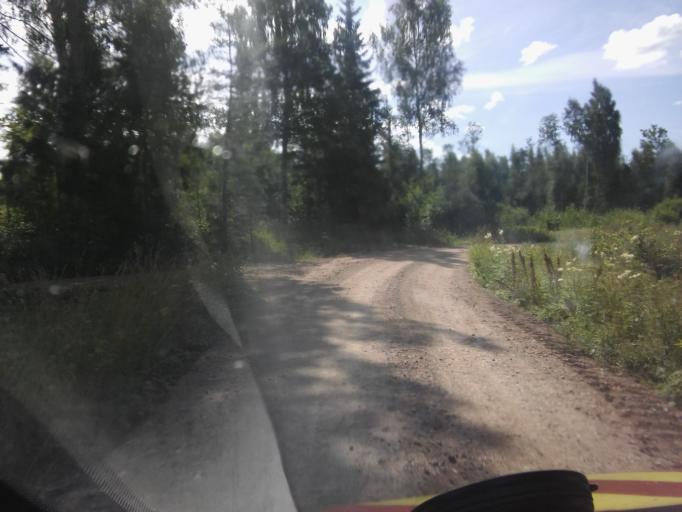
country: EE
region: Paernumaa
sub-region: Sindi linn
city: Sindi
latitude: 58.2532
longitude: 24.7643
